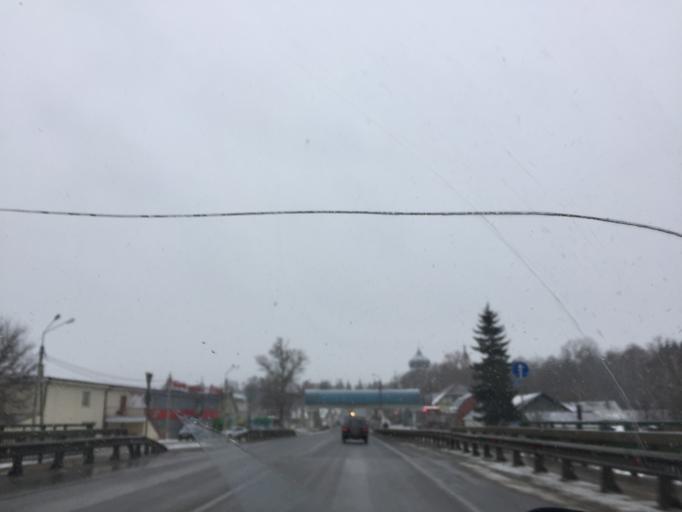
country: RU
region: Tula
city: Plavsk
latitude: 53.7117
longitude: 37.2957
